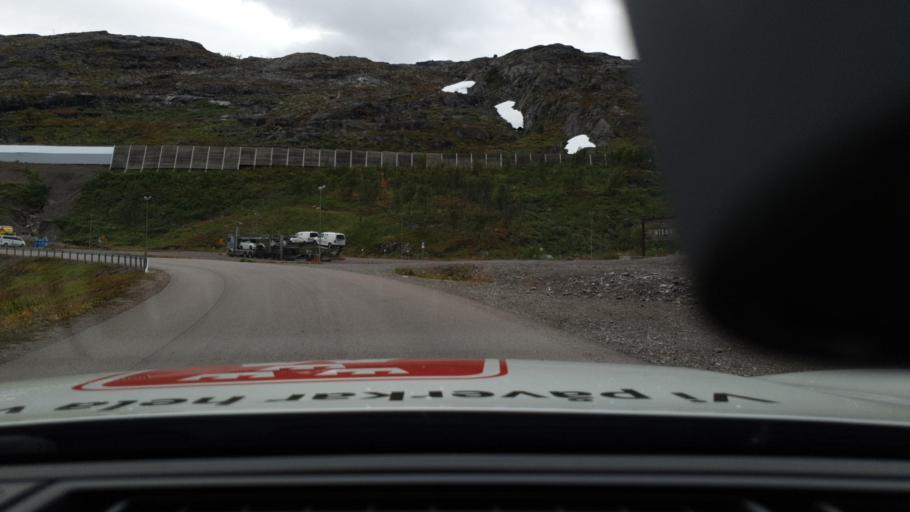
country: NO
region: Troms
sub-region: Lavangen
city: Tennevoll
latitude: 68.4299
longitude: 18.1187
